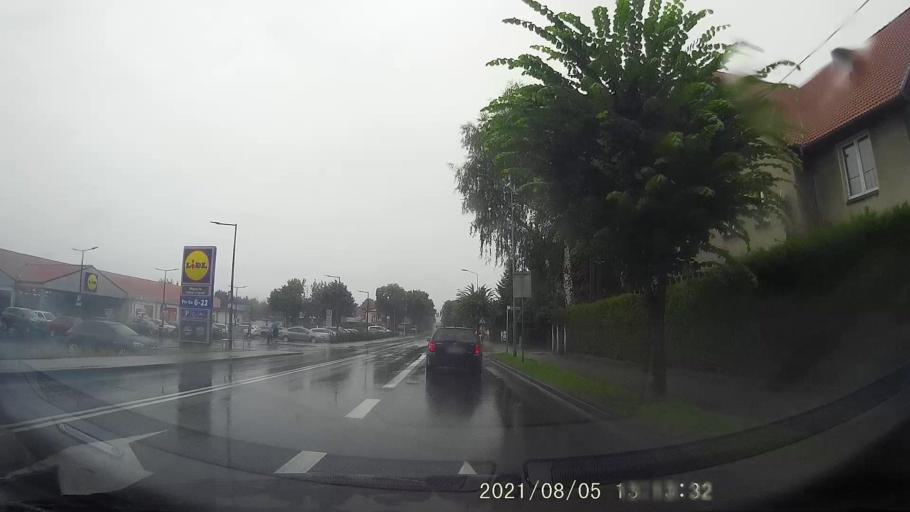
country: PL
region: Opole Voivodeship
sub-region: Powiat krapkowicki
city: Krapkowice
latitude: 50.4729
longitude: 17.9624
